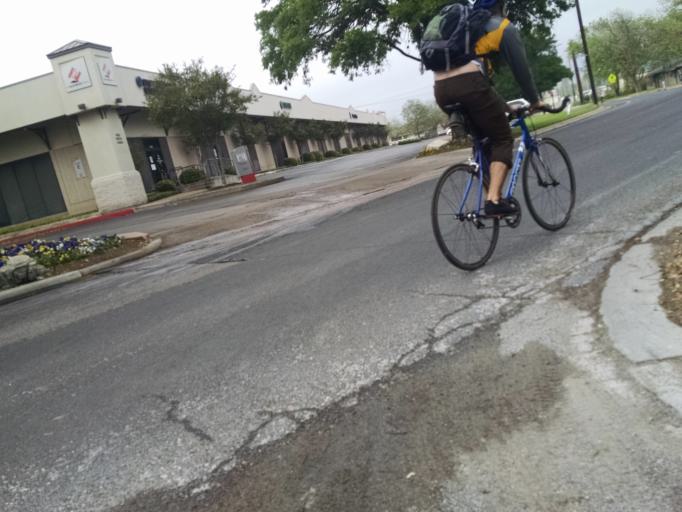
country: US
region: Texas
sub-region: Travis County
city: Austin
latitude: 30.3223
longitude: -97.7248
